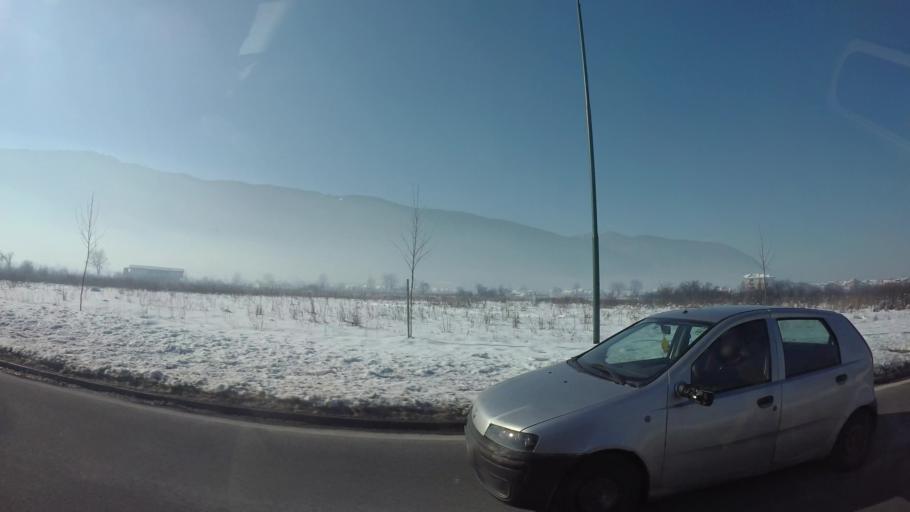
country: BA
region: Federation of Bosnia and Herzegovina
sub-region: Kanton Sarajevo
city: Sarajevo
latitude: 43.8066
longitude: 18.3111
